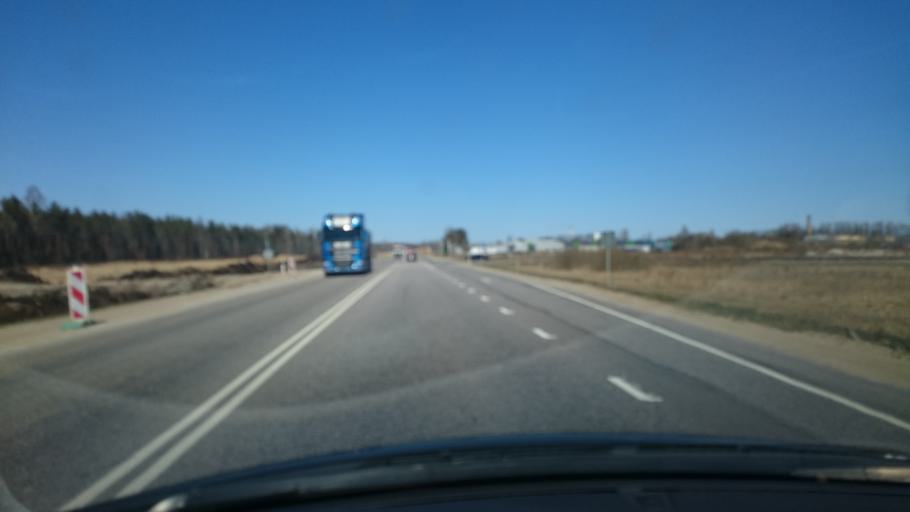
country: EE
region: Harju
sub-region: Rae vald
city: Jueri
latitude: 59.3974
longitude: 24.9175
